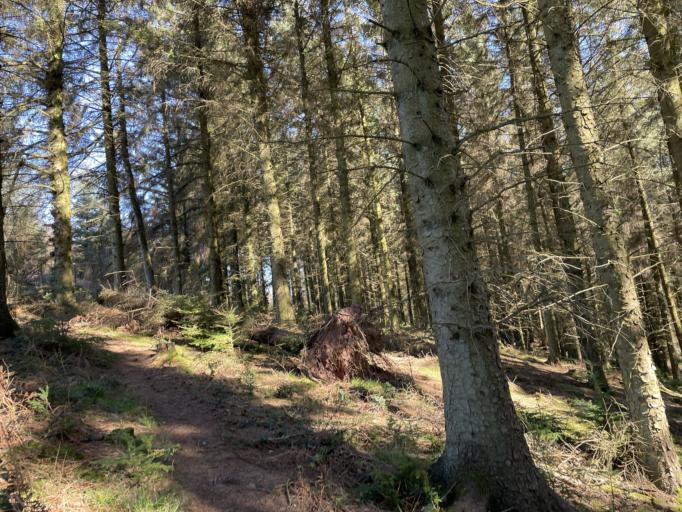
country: GB
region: England
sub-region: Somerset
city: Minehead
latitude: 51.1680
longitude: -3.4485
